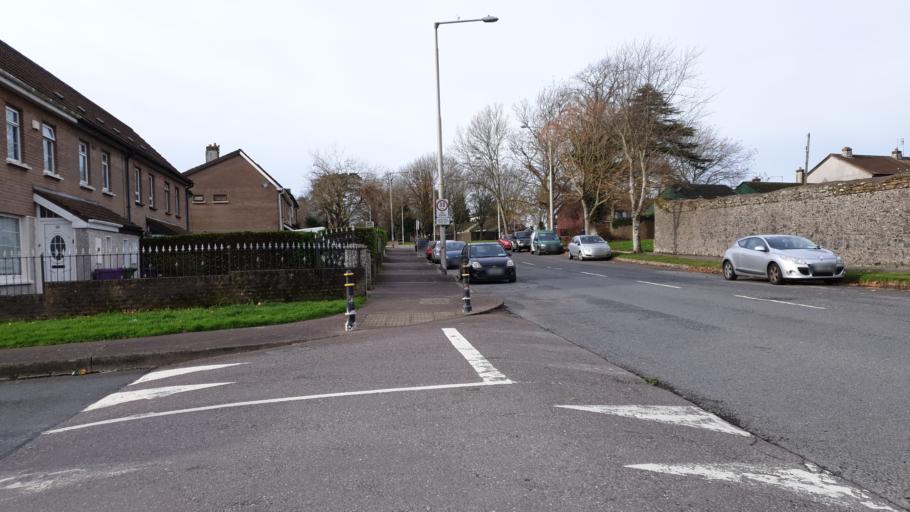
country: IE
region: Munster
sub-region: County Cork
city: Passage West
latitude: 51.8949
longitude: -8.3991
